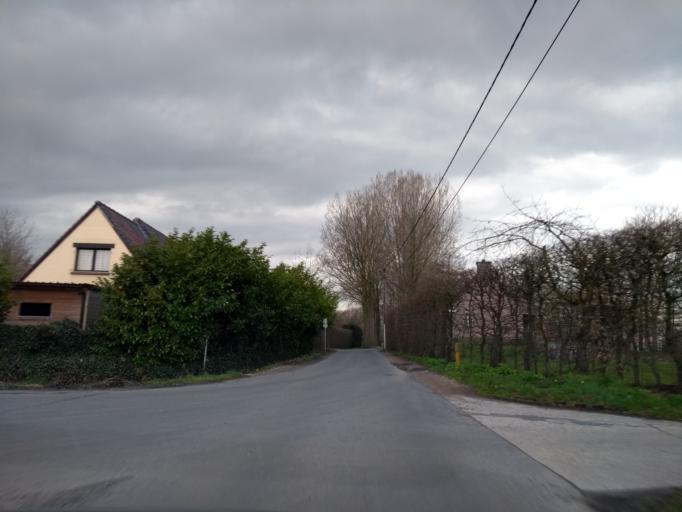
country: BE
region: Flanders
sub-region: Provincie Oost-Vlaanderen
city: Nevele
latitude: 51.0660
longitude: 3.5249
